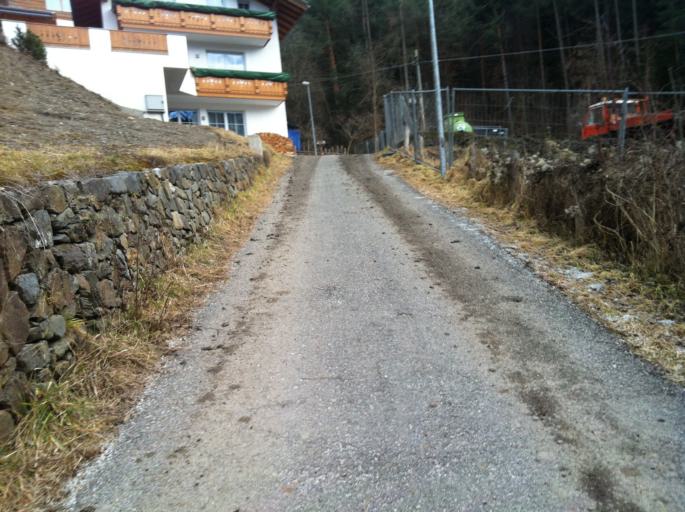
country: IT
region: Trentino-Alto Adige
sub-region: Bolzano
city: Bressanone
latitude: 46.7013
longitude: 11.6657
